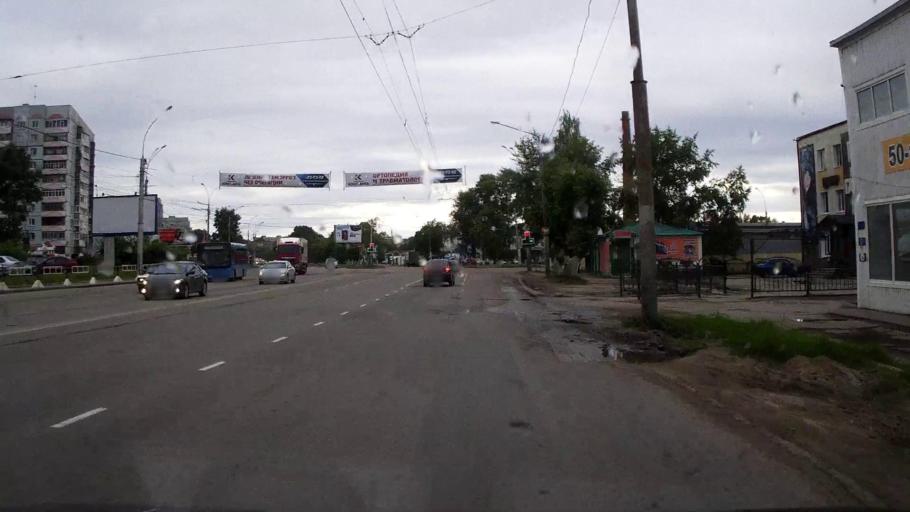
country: RU
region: Vologda
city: Vologda
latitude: 59.2038
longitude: 39.8703
